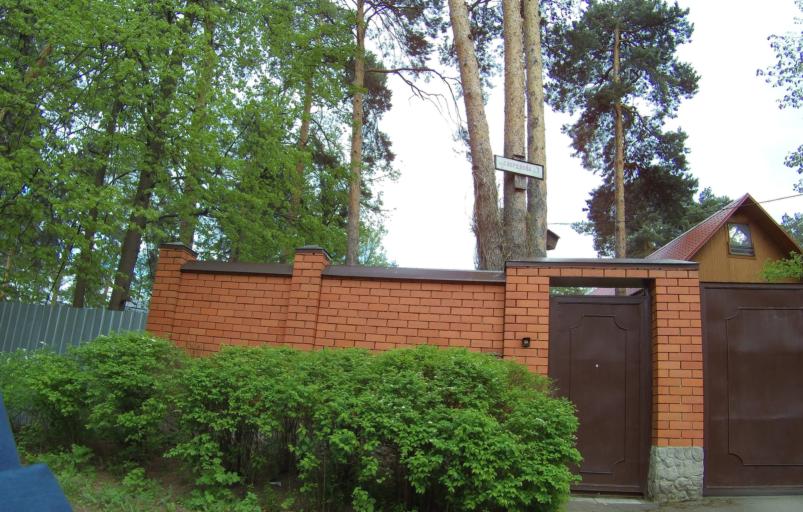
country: RU
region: Moskovskaya
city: Kratovo
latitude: 55.5869
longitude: 38.1520
